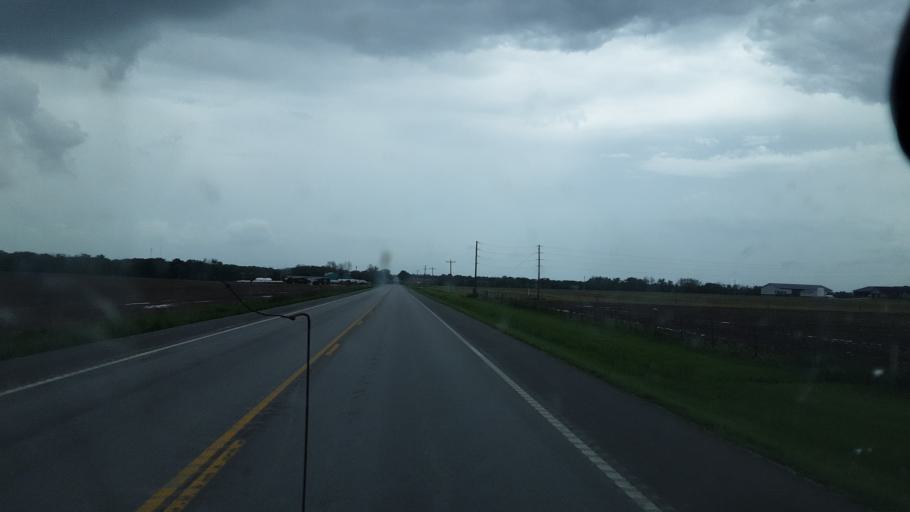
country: US
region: Missouri
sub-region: Marion County
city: Palmyra
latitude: 39.7326
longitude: -91.5099
